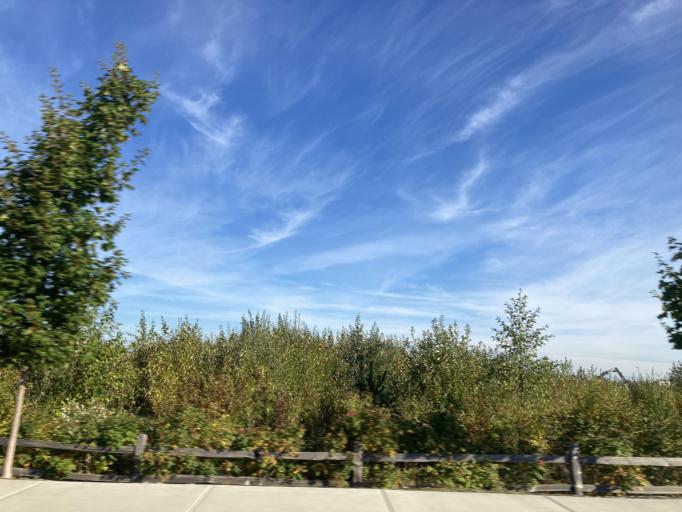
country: US
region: Washington
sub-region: Whatcom County
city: Marietta-Alderwood
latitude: 48.8151
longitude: -122.5040
